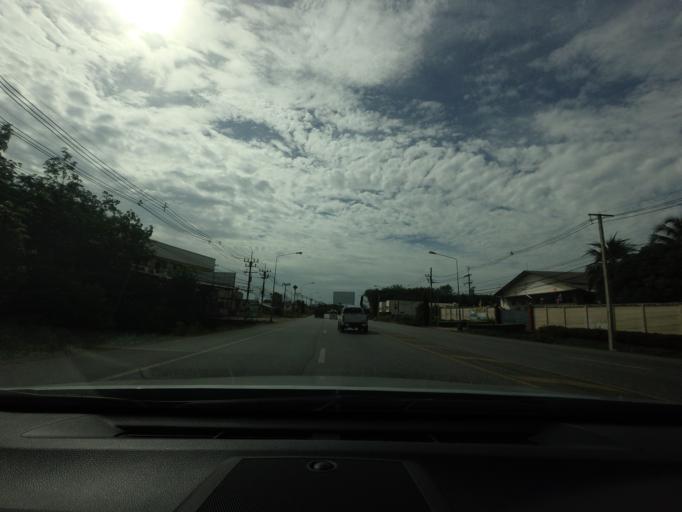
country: TH
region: Songkhla
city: Hat Yai
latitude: 6.9768
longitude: 100.4271
